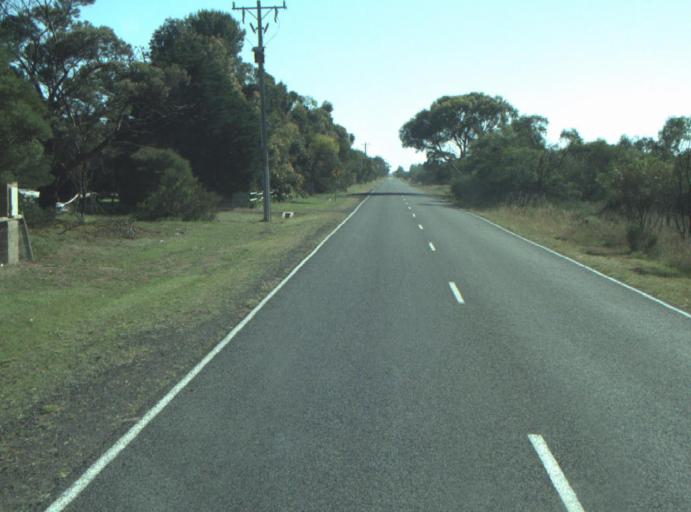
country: AU
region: Victoria
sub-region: Greater Geelong
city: Lara
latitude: -38.0074
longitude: 144.4323
